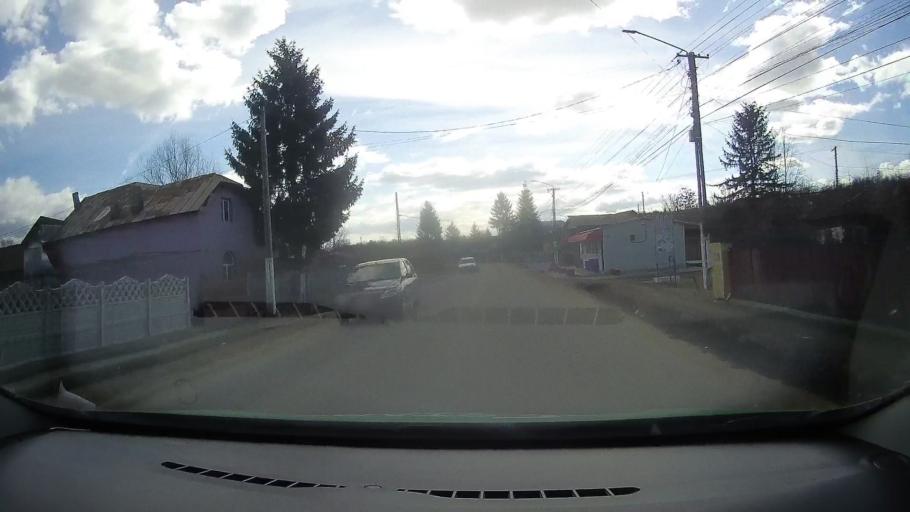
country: RO
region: Dambovita
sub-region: Comuna Doicesti
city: Doicesti
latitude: 44.9758
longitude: 25.3923
